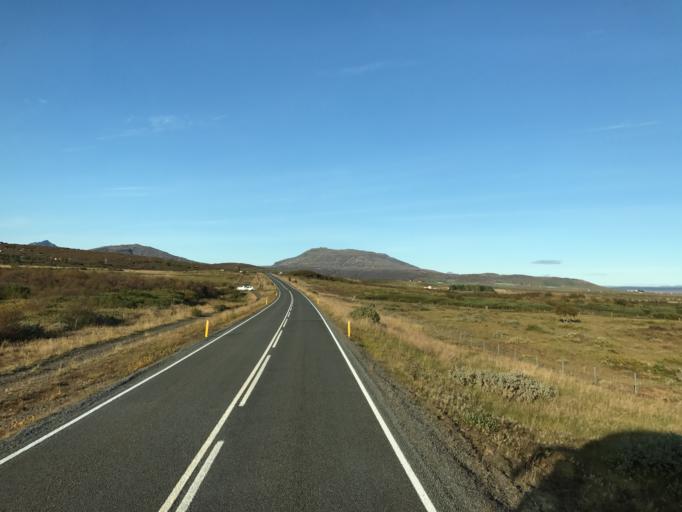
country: IS
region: South
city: Selfoss
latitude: 64.2469
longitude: -20.4965
